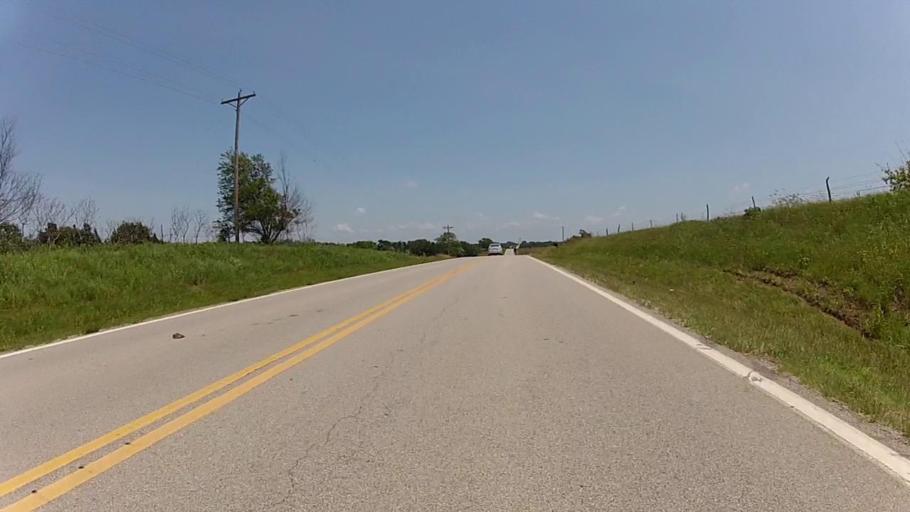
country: US
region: Kansas
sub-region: Montgomery County
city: Cherryvale
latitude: 37.1937
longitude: -95.5244
